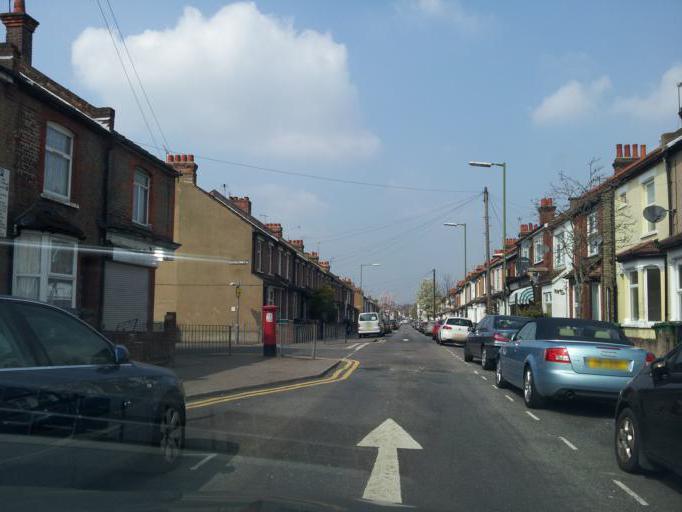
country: GB
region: England
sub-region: Hertfordshire
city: Watford
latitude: 51.6508
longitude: -0.4054
